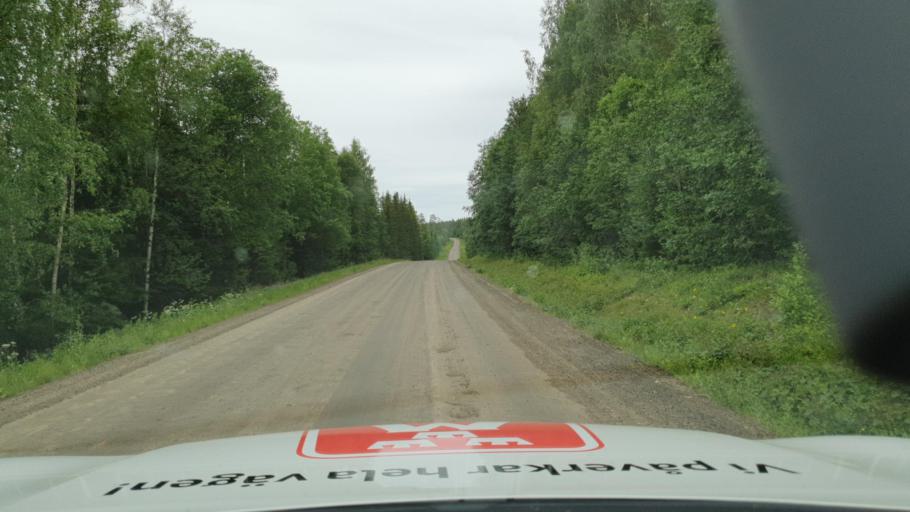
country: SE
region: Vaesterbotten
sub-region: Skelleftea Kommun
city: Burtraesk
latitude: 64.3374
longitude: 20.6093
